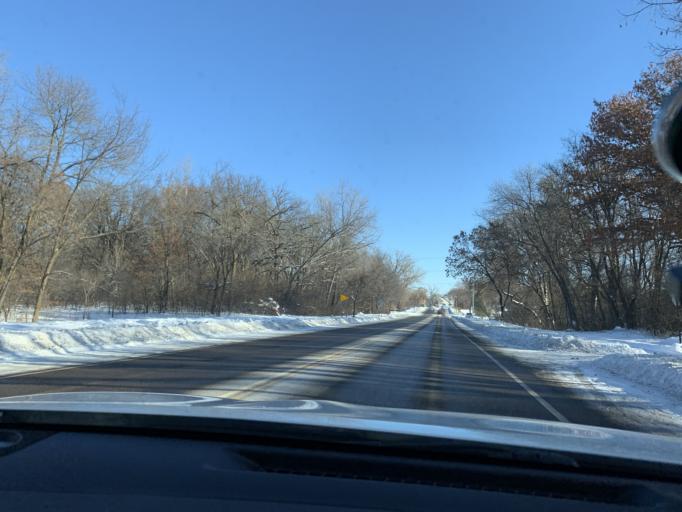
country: US
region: Minnesota
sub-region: Anoka County
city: Coon Rapids
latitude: 45.1609
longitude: -93.2980
